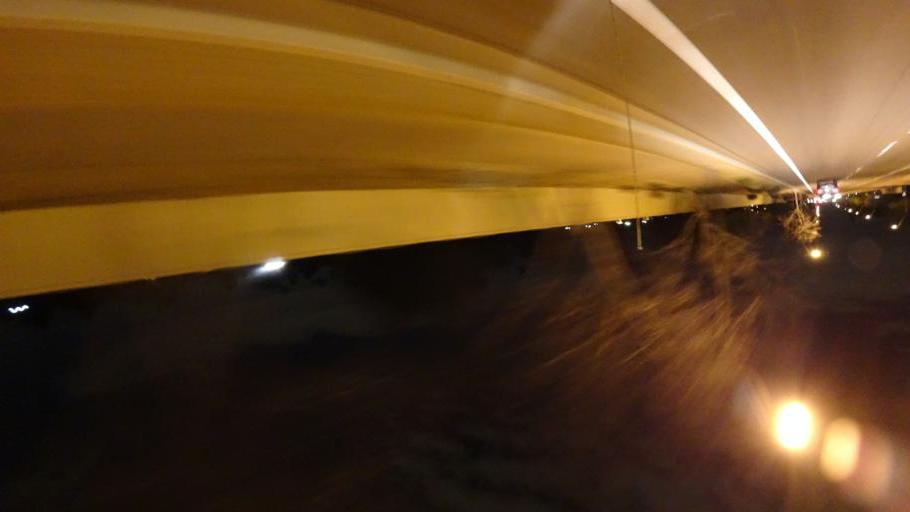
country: US
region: Arizona
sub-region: Maricopa County
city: Guadalupe
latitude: 33.3431
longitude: -111.9112
